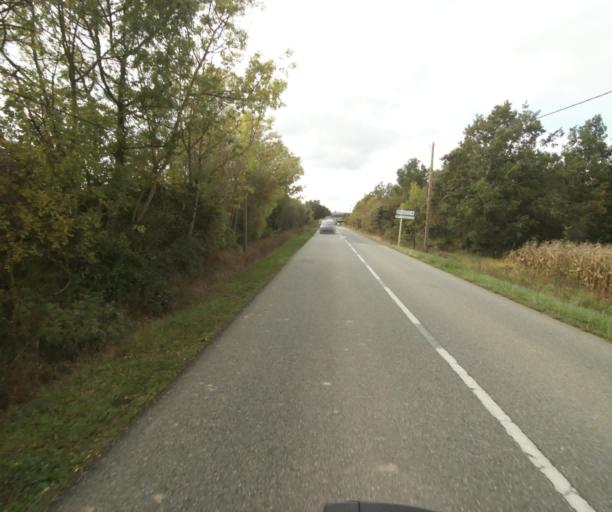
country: FR
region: Midi-Pyrenees
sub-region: Departement du Tarn-et-Garonne
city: Verdun-sur-Garonne
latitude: 43.8505
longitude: 1.1411
